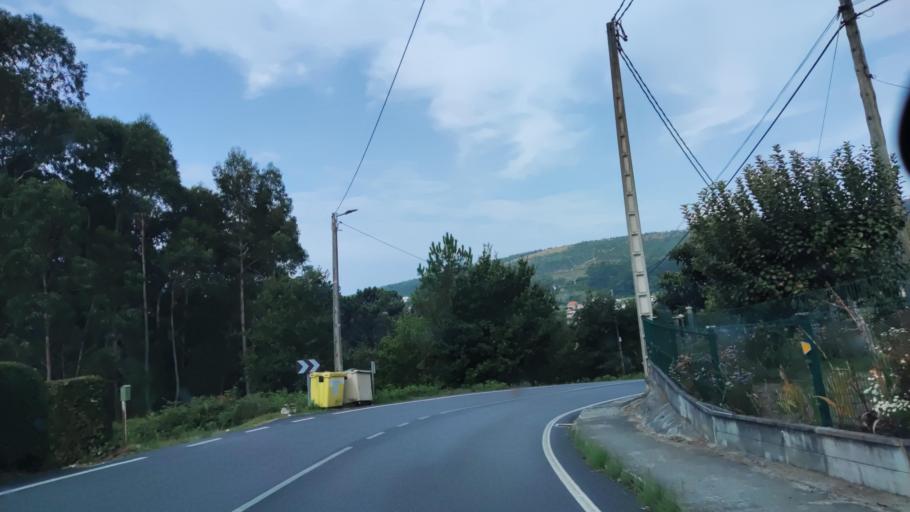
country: ES
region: Galicia
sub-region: Provincia de Pontevedra
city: Catoira
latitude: 42.6532
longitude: -8.7661
